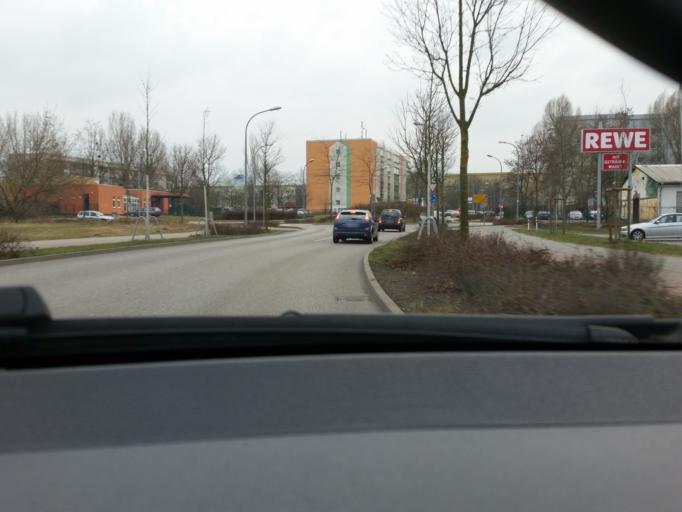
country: DE
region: Brandenburg
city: Teltow
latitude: 52.4010
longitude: 13.2725
